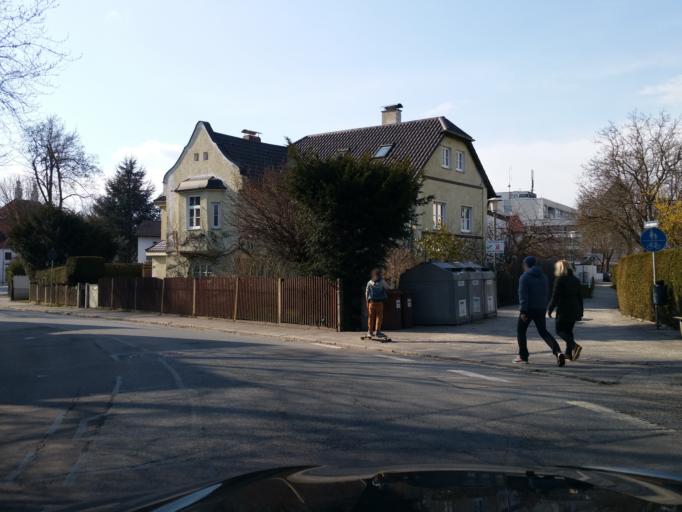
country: DE
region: Bavaria
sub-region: Lower Bavaria
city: Landshut
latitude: 48.5264
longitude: 12.1643
